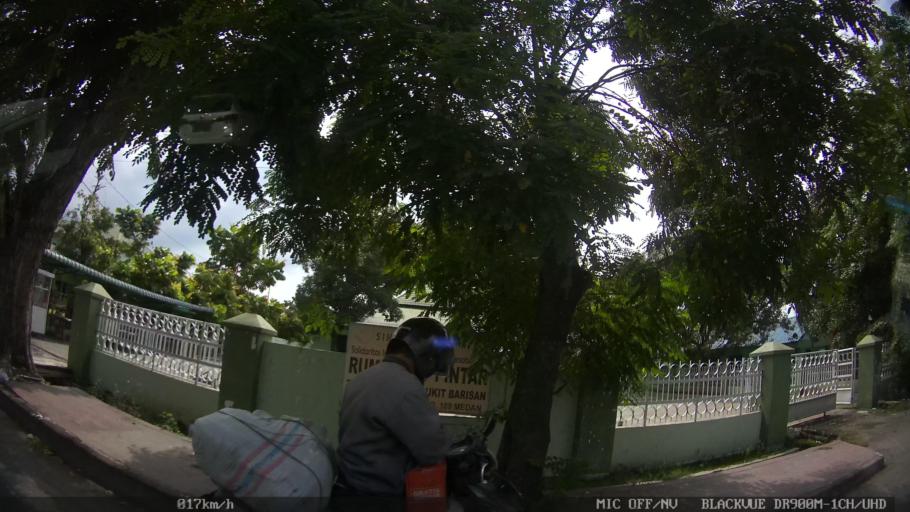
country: ID
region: North Sumatra
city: Medan
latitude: 3.6055
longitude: 98.6449
